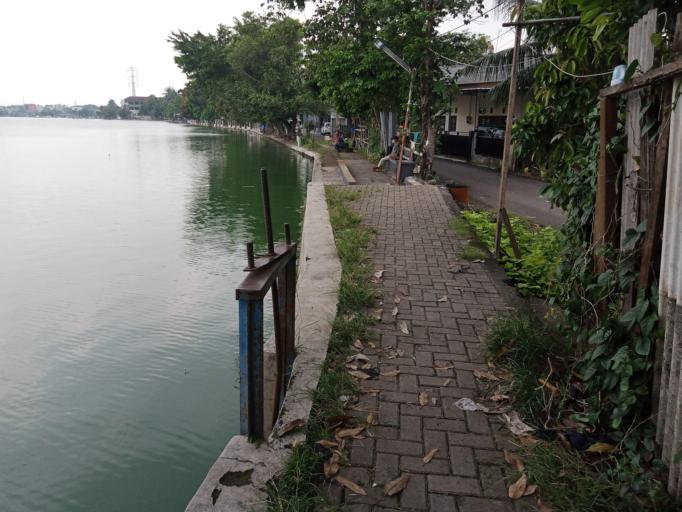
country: ID
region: West Java
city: Depok
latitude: -6.3907
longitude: 106.8166
